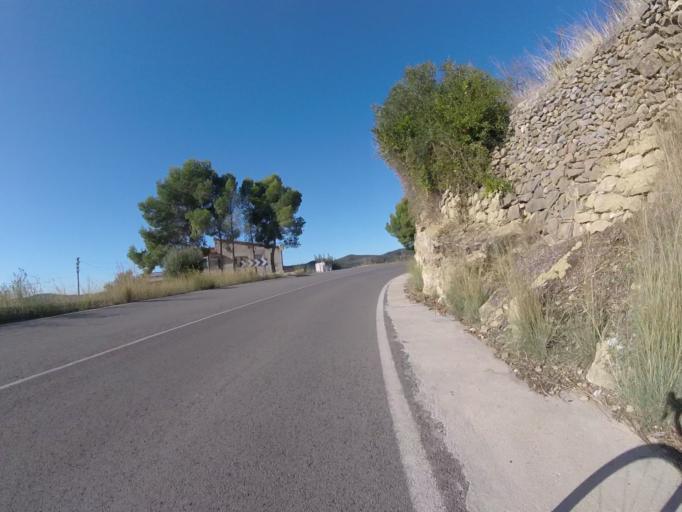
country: ES
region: Valencia
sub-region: Provincia de Castello
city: Cervera del Maestre
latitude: 40.4565
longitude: 0.2700
